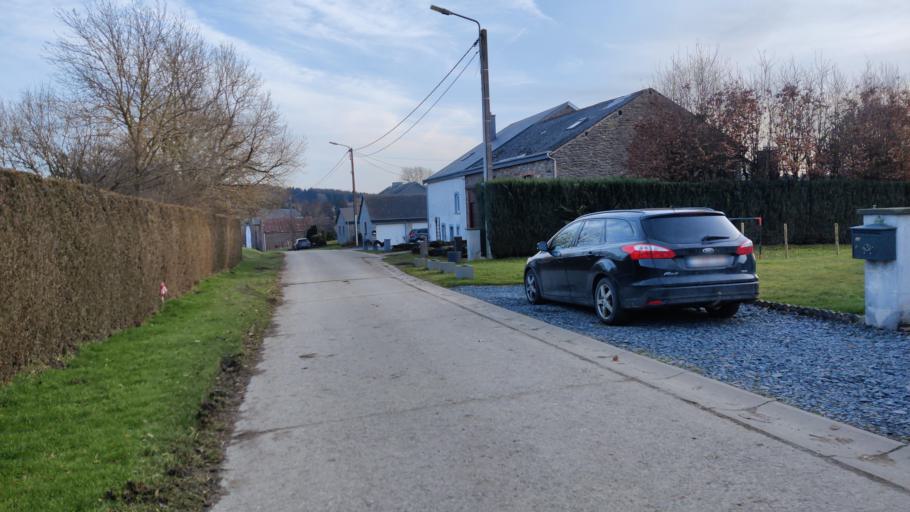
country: BE
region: Wallonia
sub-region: Province du Luxembourg
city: Houffalize
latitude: 50.1111
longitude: 5.8374
